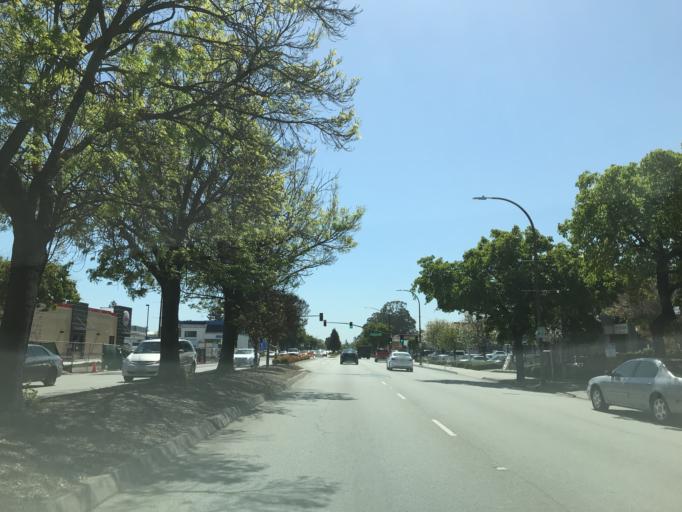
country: US
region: California
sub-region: San Mateo County
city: Redwood City
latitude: 37.4895
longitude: -122.2388
